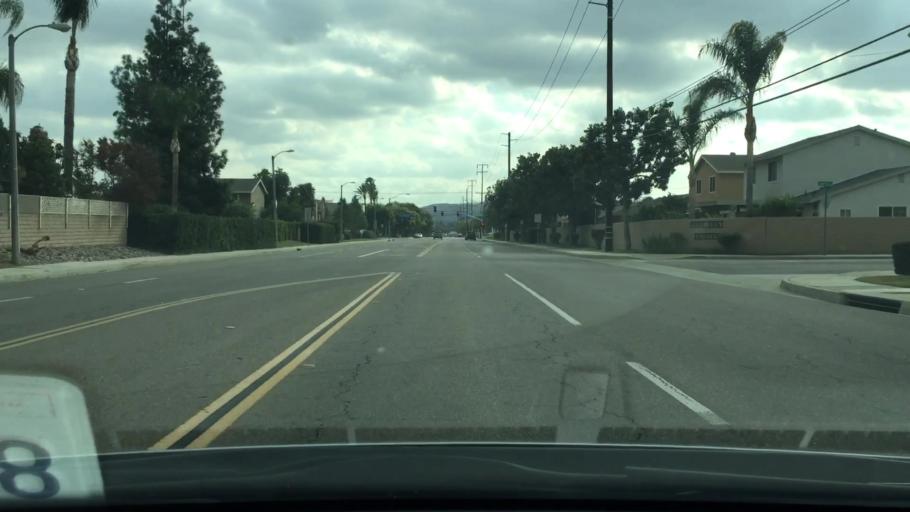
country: US
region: California
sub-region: San Bernardino County
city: Chino
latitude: 34.0064
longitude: -117.7154
